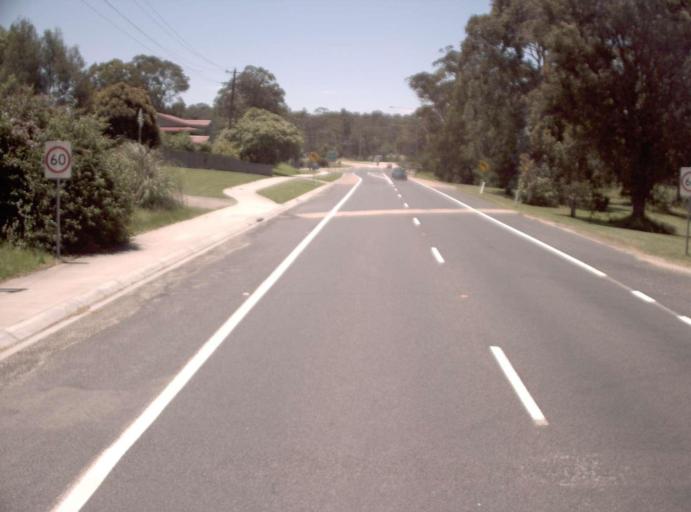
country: AU
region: Victoria
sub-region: East Gippsland
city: Lakes Entrance
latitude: -37.7336
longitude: 148.0896
